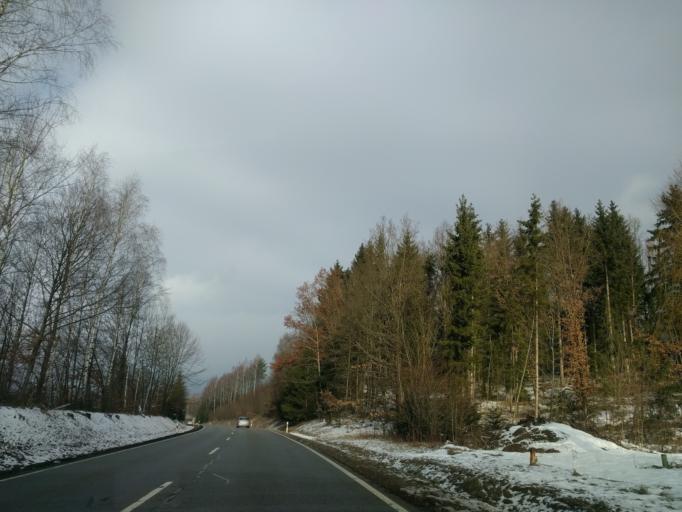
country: DE
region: Bavaria
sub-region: Lower Bavaria
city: Zwiesel
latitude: 49.0254
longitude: 13.2456
